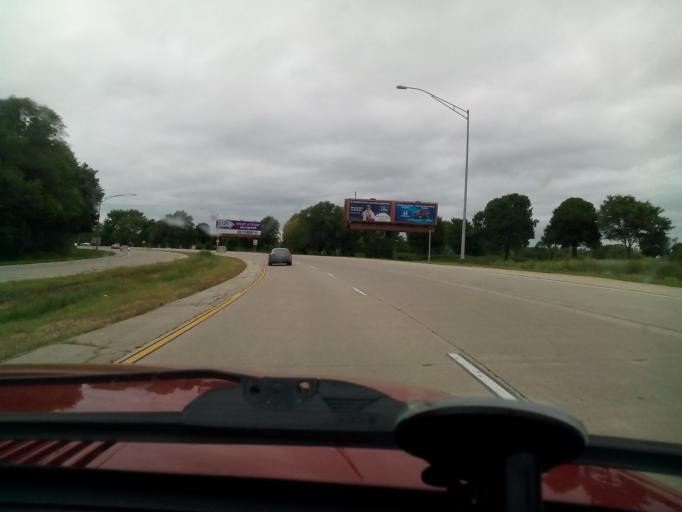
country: US
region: Wisconsin
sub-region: Dane County
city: Maple Bluff
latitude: 43.1095
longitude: -89.3414
